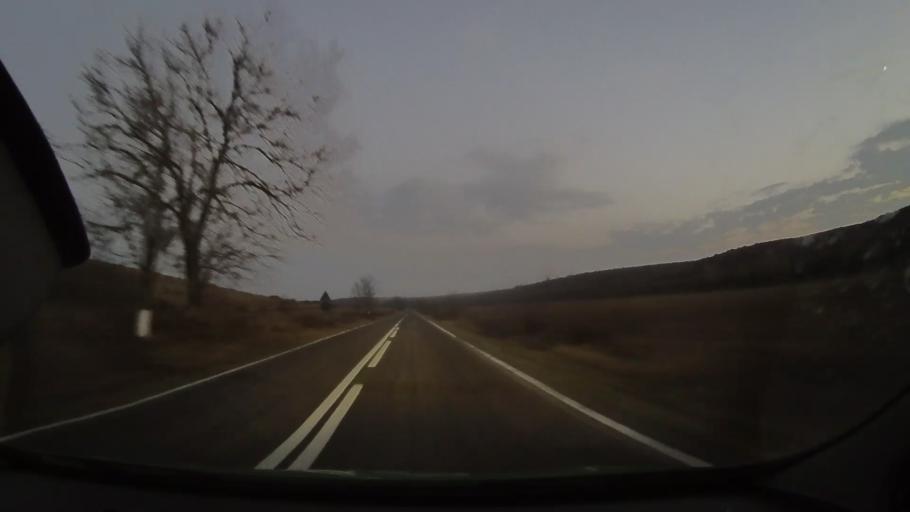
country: RO
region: Constanta
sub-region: Comuna Ion Corvin
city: Ion Corvin
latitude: 44.1092
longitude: 27.7761
